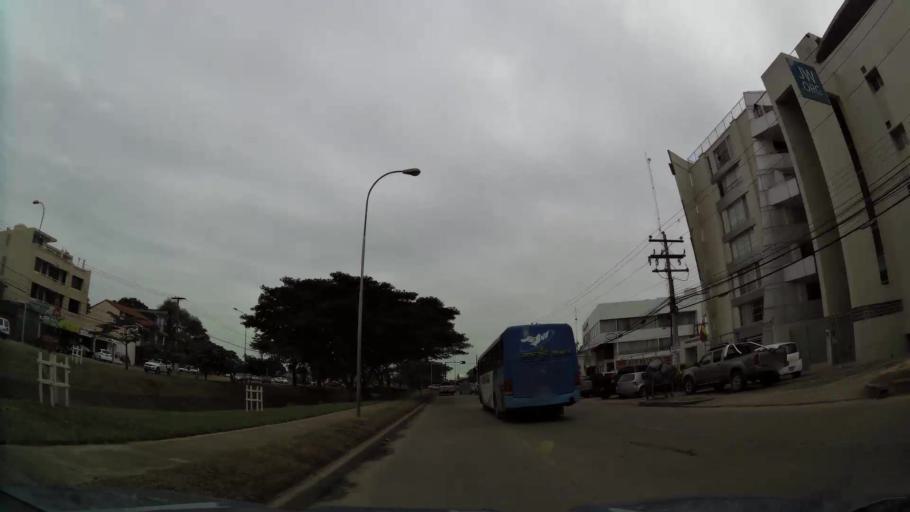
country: BO
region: Santa Cruz
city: Santa Cruz de la Sierra
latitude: -17.7509
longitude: -63.1678
